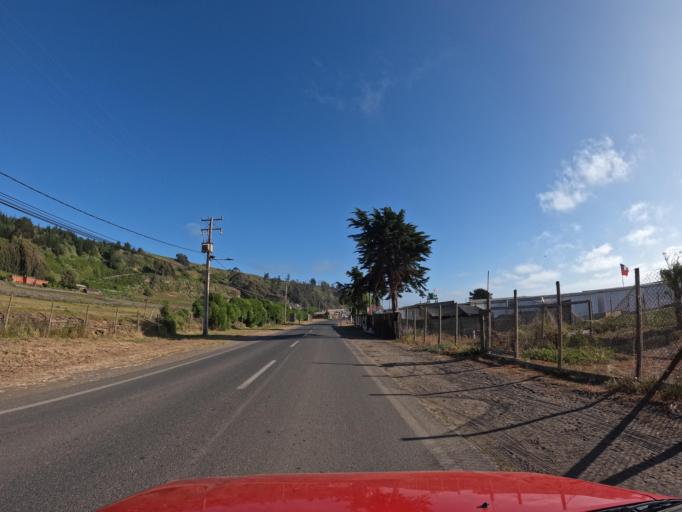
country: CL
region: Maule
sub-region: Provincia de Talca
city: Constitucion
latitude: -34.9010
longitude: -72.1795
